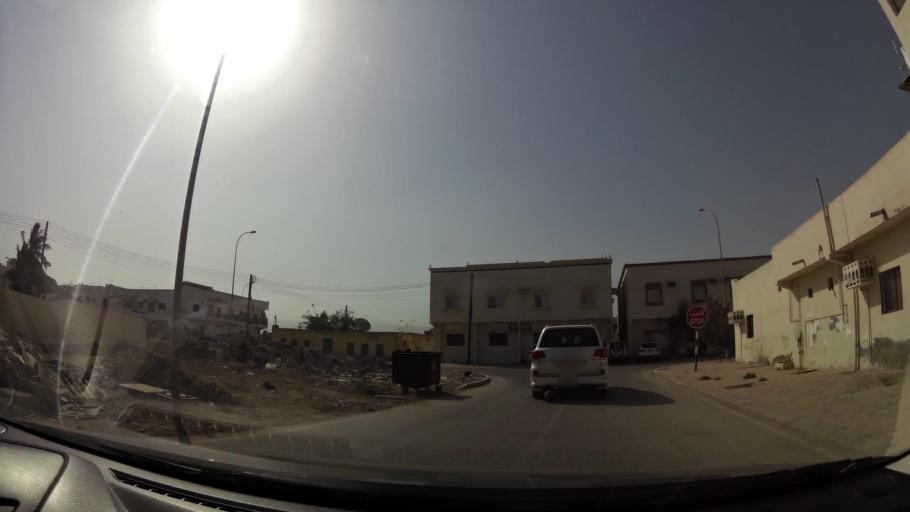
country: OM
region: Zufar
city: Salalah
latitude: 16.9985
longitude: 54.0373
